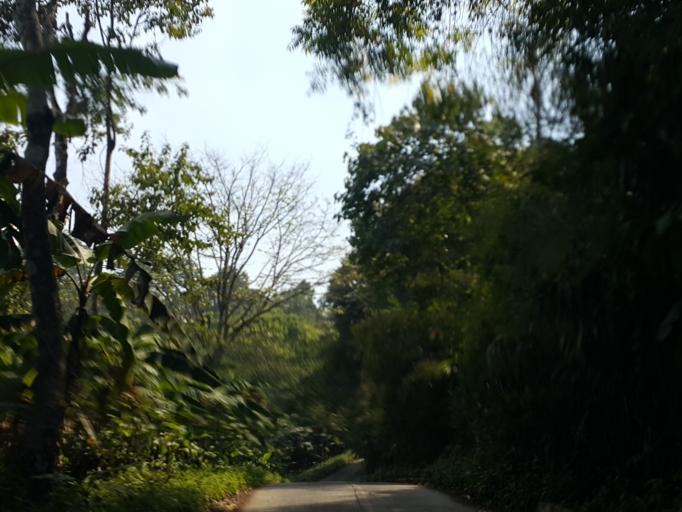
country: TH
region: Chiang Mai
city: Mae On
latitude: 18.8548
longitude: 99.3645
